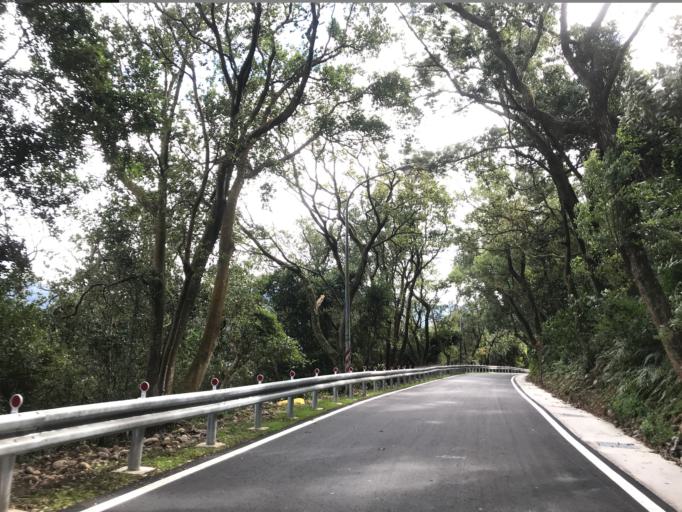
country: TW
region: Taiwan
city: Daxi
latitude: 24.8390
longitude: 121.2451
